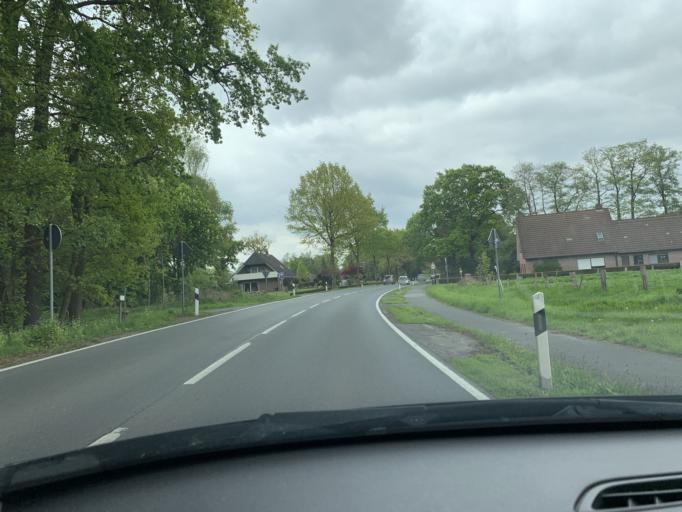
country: DE
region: Lower Saxony
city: Bad Zwischenahn
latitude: 53.2175
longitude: 8.0094
